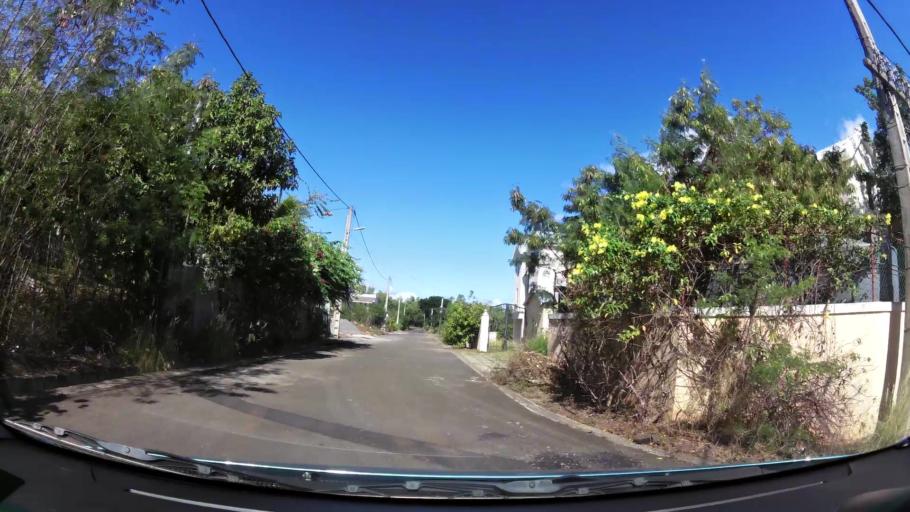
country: MU
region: Black River
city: Flic en Flac
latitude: -20.2843
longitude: 57.3738
